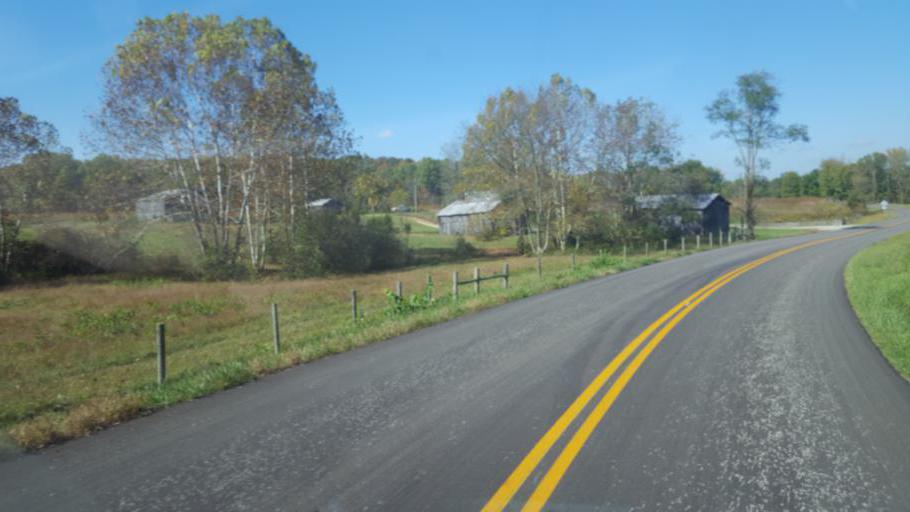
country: US
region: Kentucky
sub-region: Fleming County
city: Flemingsburg
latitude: 38.4588
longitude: -83.5839
